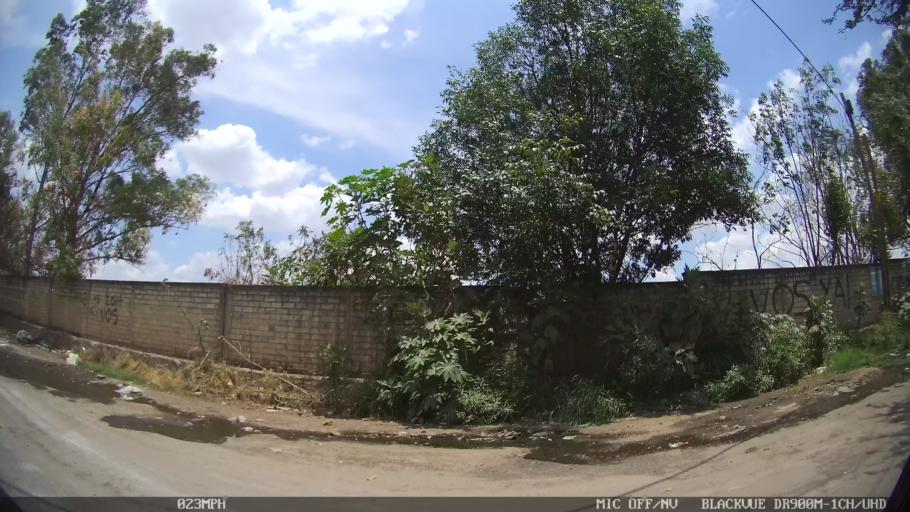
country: MX
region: Jalisco
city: Tonala
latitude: 20.6297
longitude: -103.2236
